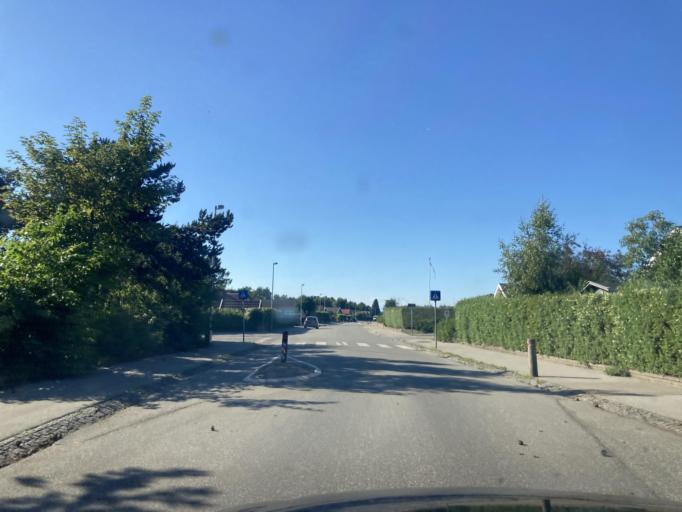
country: DK
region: Capital Region
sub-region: Halsnaes Kommune
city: Frederiksvaerk
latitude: 55.9822
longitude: 12.0074
